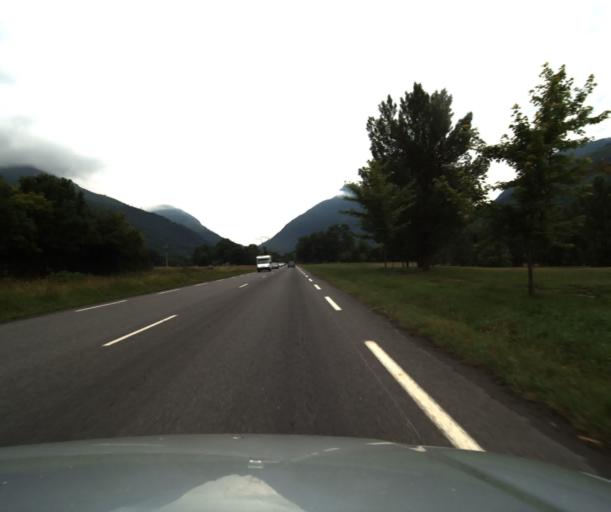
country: FR
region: Midi-Pyrenees
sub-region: Departement des Hautes-Pyrenees
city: Pierrefitte-Nestalas
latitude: 42.9880
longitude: -0.0727
